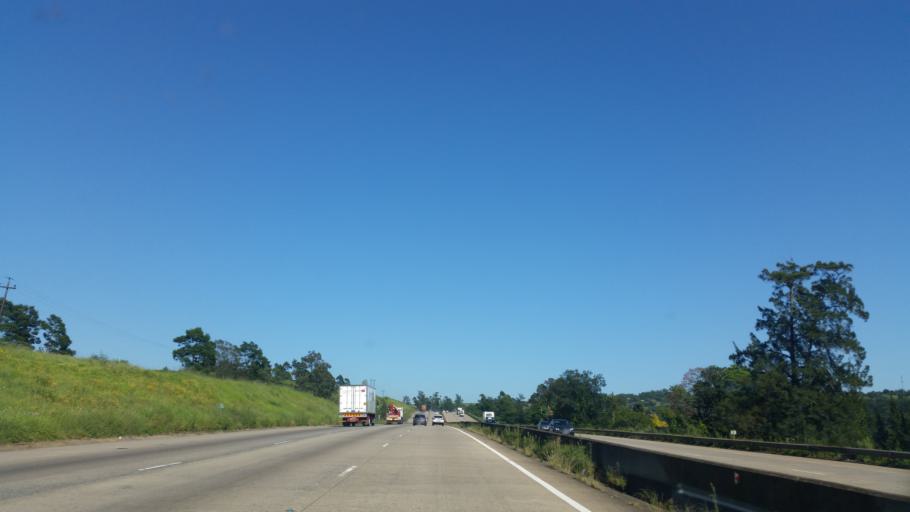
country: ZA
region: KwaZulu-Natal
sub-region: eThekwini Metropolitan Municipality
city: Mpumalanga
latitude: -29.7398
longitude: 30.6565
